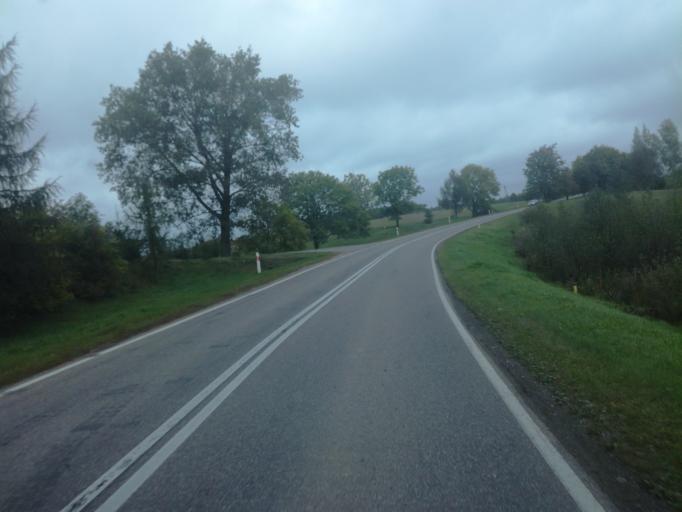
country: PL
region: Podlasie
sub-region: Powiat sejnenski
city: Sejny
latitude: 54.1211
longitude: 23.4308
